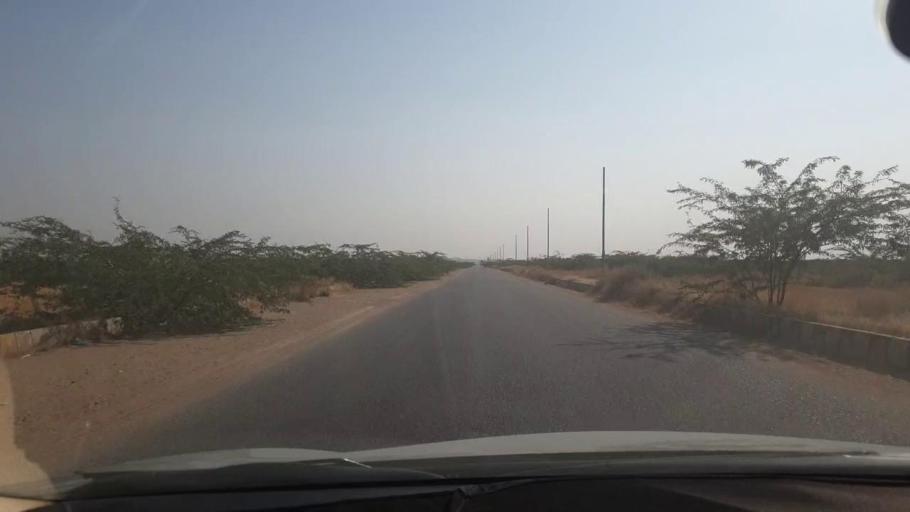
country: PK
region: Sindh
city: Malir Cantonment
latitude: 25.0670
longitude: 67.1389
